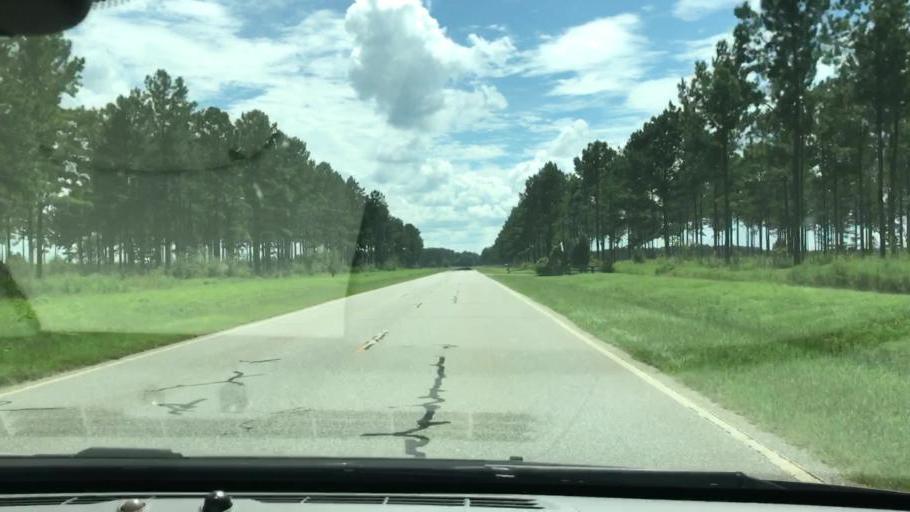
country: US
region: Georgia
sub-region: Quitman County
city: Georgetown
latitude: 32.0604
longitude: -85.0363
